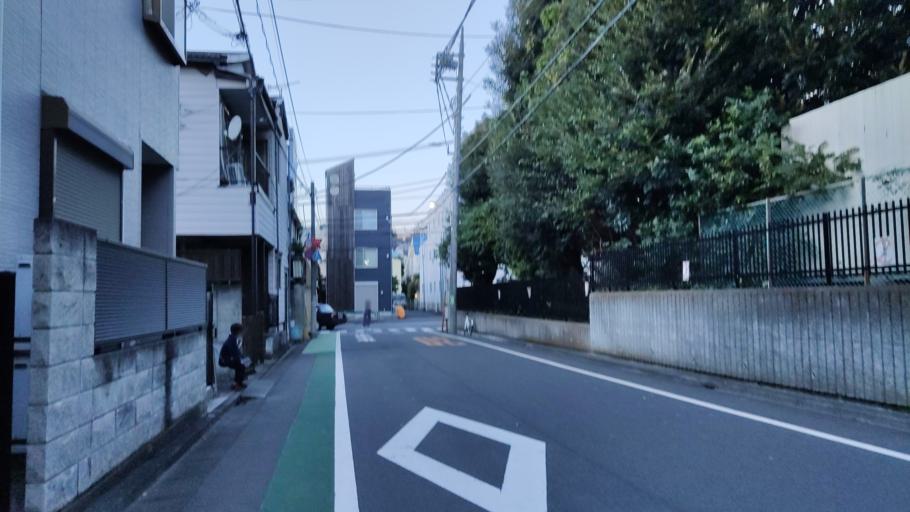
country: JP
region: Tokyo
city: Tokyo
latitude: 35.6553
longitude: 139.6802
